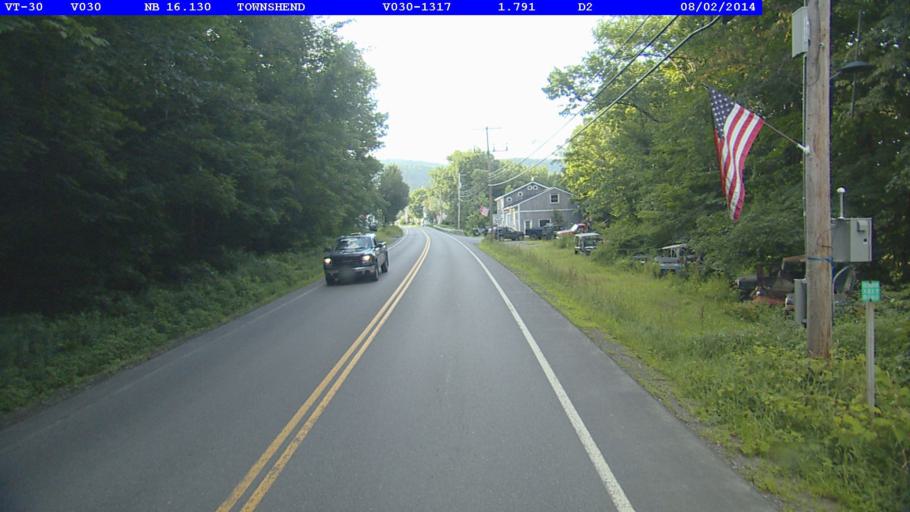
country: US
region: Vermont
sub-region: Windham County
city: Newfane
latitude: 43.0431
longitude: -72.6650
